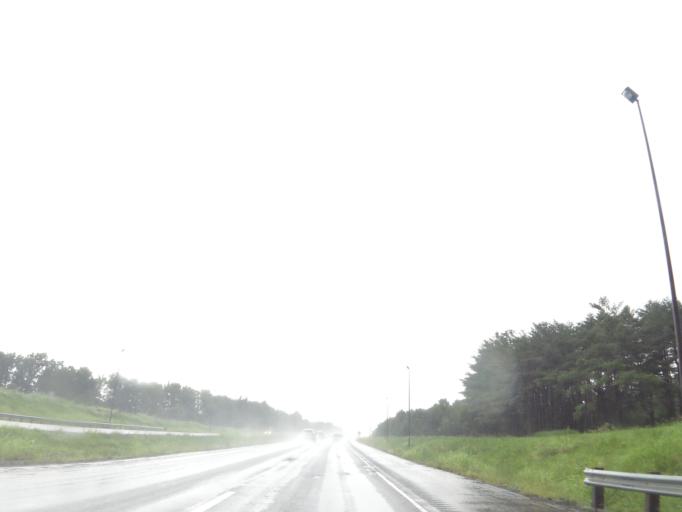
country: US
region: Illinois
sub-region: Franklin County
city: West Frankfort
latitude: 37.8979
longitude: -88.9462
